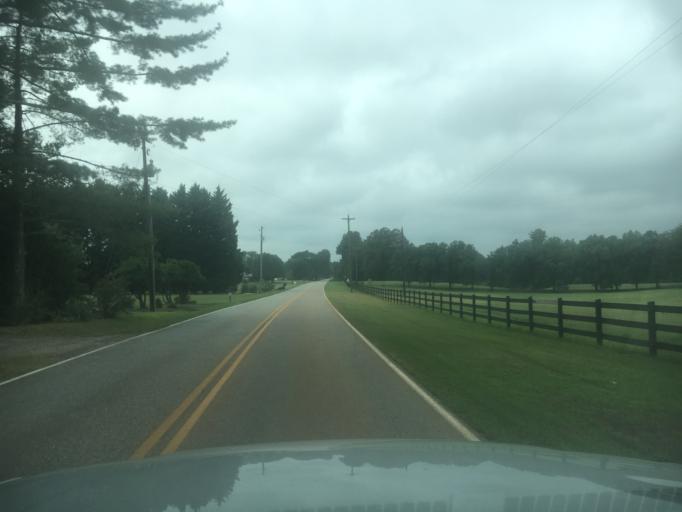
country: US
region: South Carolina
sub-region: Spartanburg County
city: Landrum
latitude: 35.1631
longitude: -82.0915
